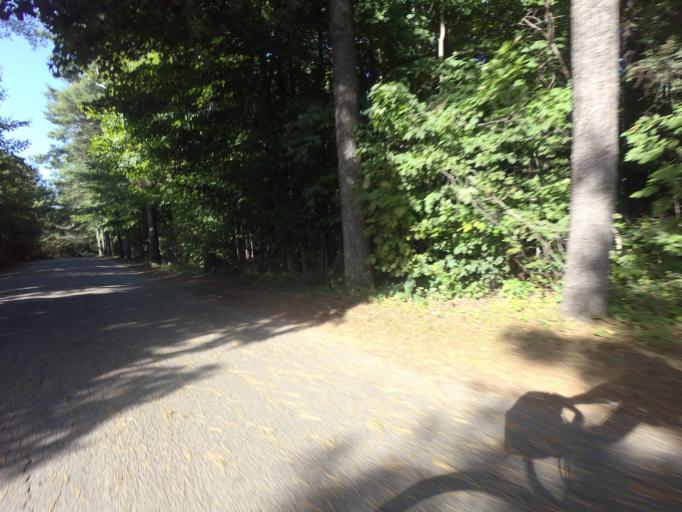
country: CA
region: Ontario
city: Waterloo
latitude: 43.6717
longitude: -80.4480
